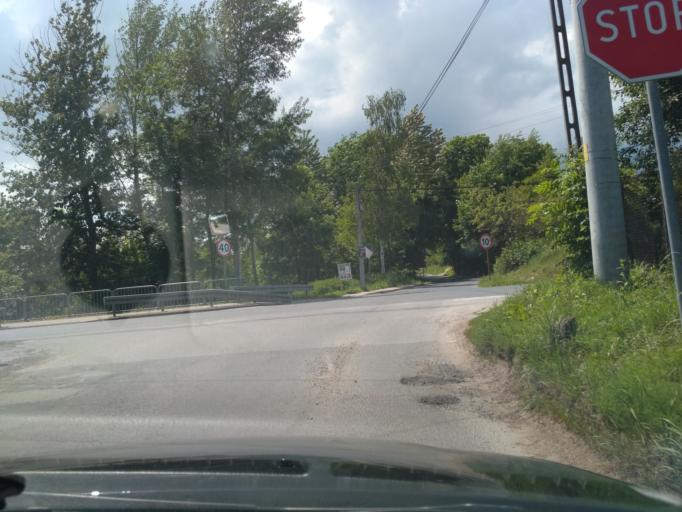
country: PL
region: Subcarpathian Voivodeship
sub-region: Powiat lancucki
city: Sonina
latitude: 50.0565
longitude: 22.2676
